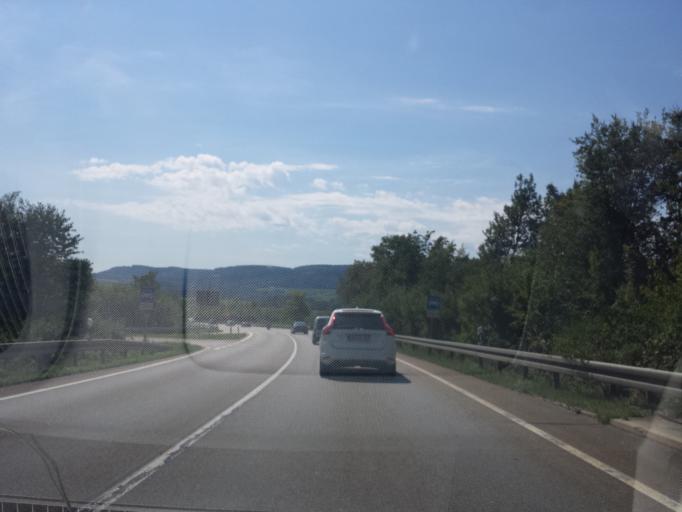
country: DE
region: Bavaria
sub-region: Lower Bavaria
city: Loitzendorf
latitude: 49.0886
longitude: 12.6412
